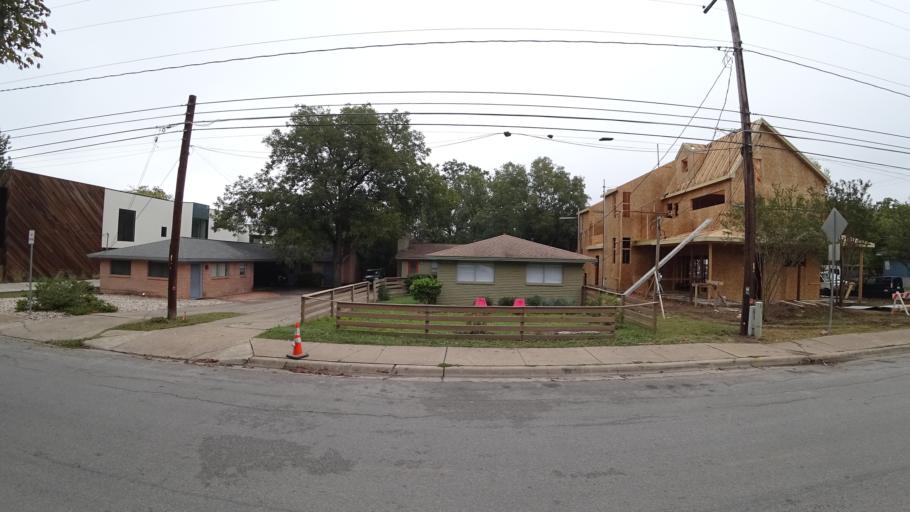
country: US
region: Texas
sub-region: Travis County
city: Rollingwood
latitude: 30.2541
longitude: -97.7725
